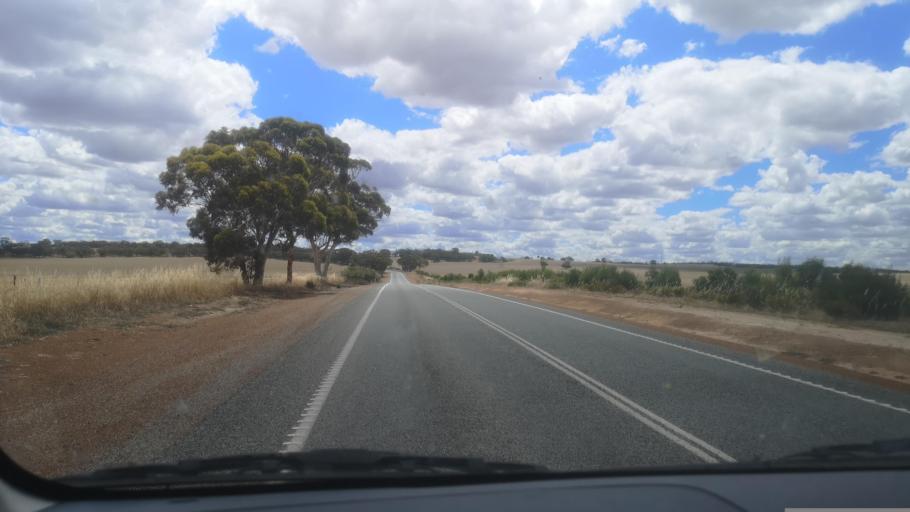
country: AU
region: Western Australia
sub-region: Beverley
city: Beverley
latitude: -32.0176
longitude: 117.2397
